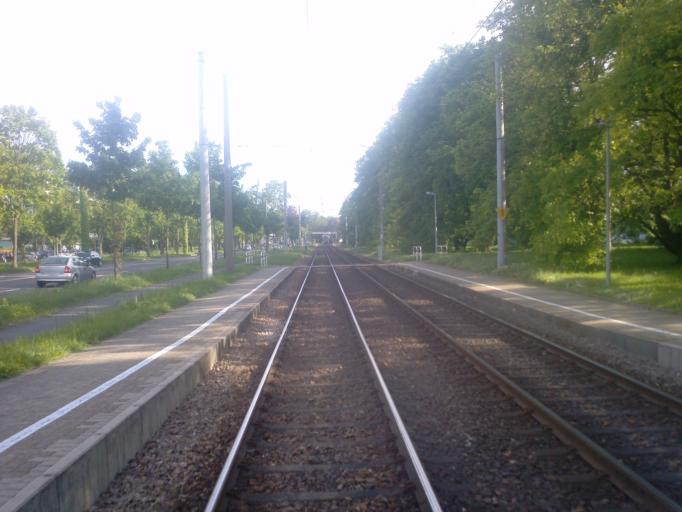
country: DE
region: Baden-Wuerttemberg
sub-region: Karlsruhe Region
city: Karlsruhe
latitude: 48.9841
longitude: 8.4036
